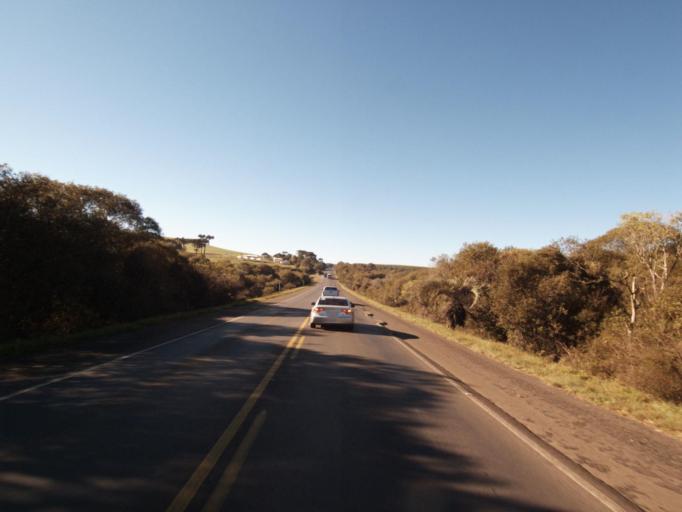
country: BR
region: Santa Catarina
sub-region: Concordia
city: Concordia
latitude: -26.9092
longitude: -51.9680
